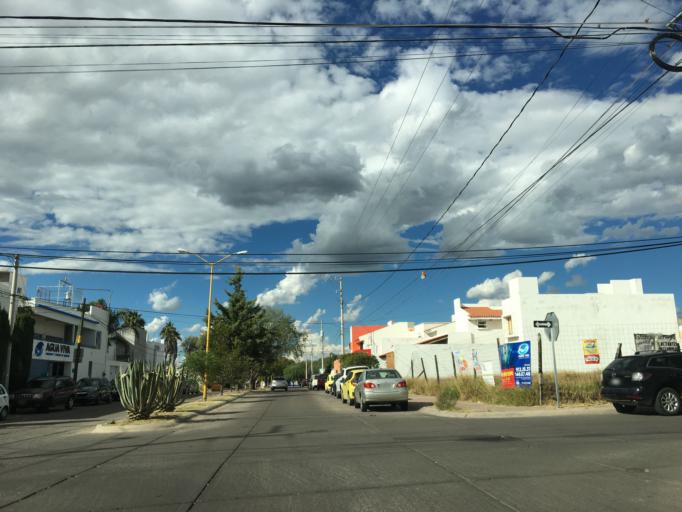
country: MX
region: Aguascalientes
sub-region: Jesus Maria
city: El Llano
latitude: 21.9285
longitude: -102.3016
